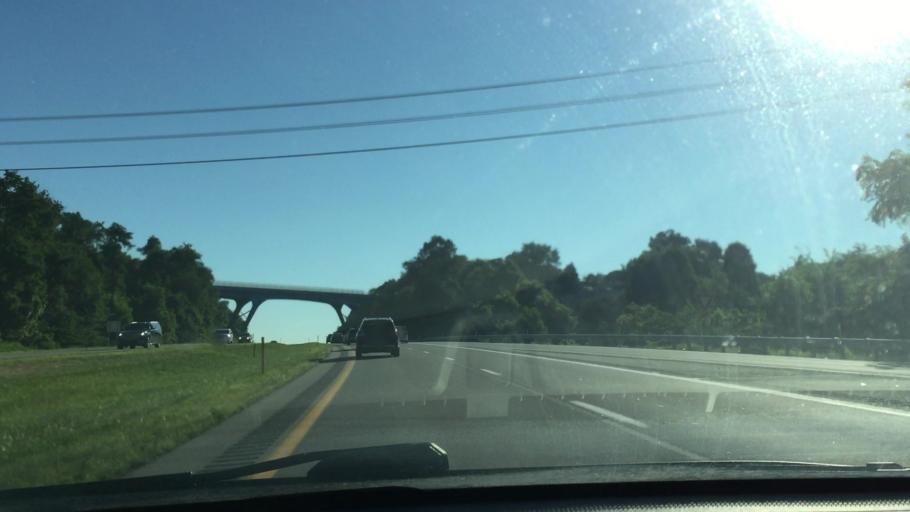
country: US
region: Pennsylvania
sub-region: Washington County
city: Houston
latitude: 40.2472
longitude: -80.1970
